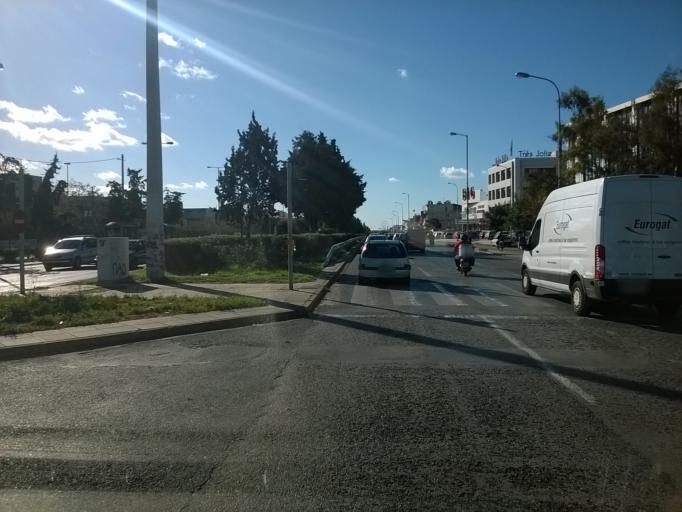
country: GR
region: Attica
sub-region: Nomarchia Athinas
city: Agios Dimitrios
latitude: 37.9238
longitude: 23.7443
